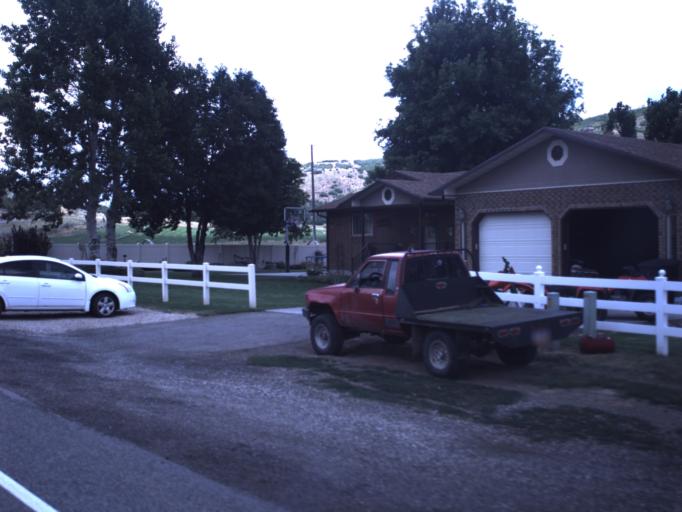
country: US
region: Utah
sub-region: Juab County
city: Nephi
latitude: 39.7178
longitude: -111.7285
